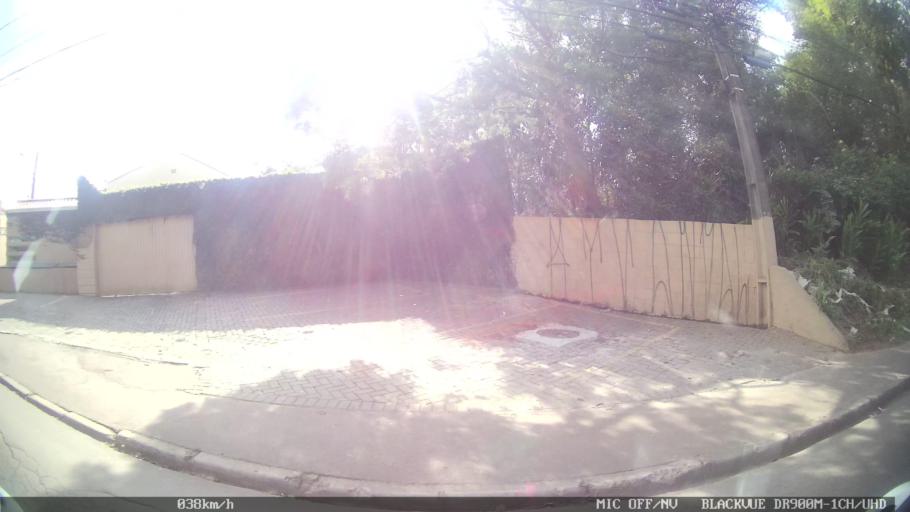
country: BR
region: Parana
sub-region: Colombo
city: Colombo
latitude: -25.3638
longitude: -49.2124
